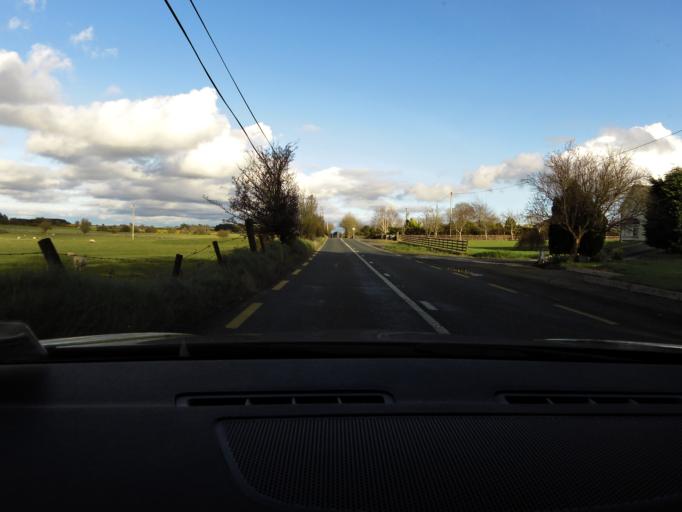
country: IE
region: Connaught
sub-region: Roscommon
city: Roscommon
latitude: 53.6514
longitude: -8.2429
